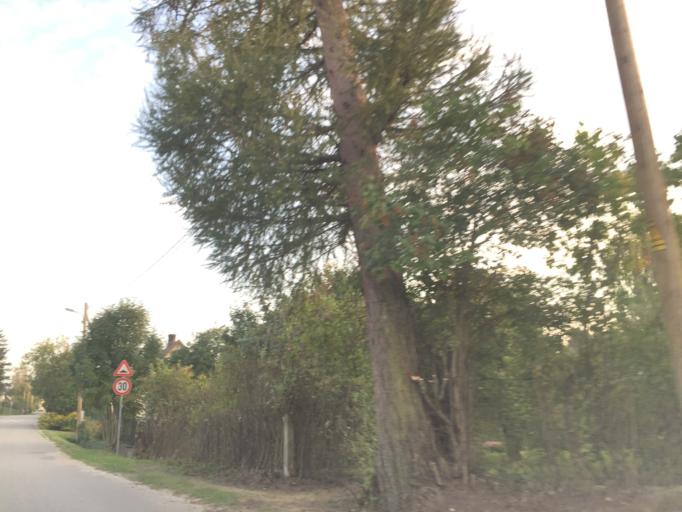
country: LV
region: Baldone
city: Baldone
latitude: 56.7474
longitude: 24.3903
